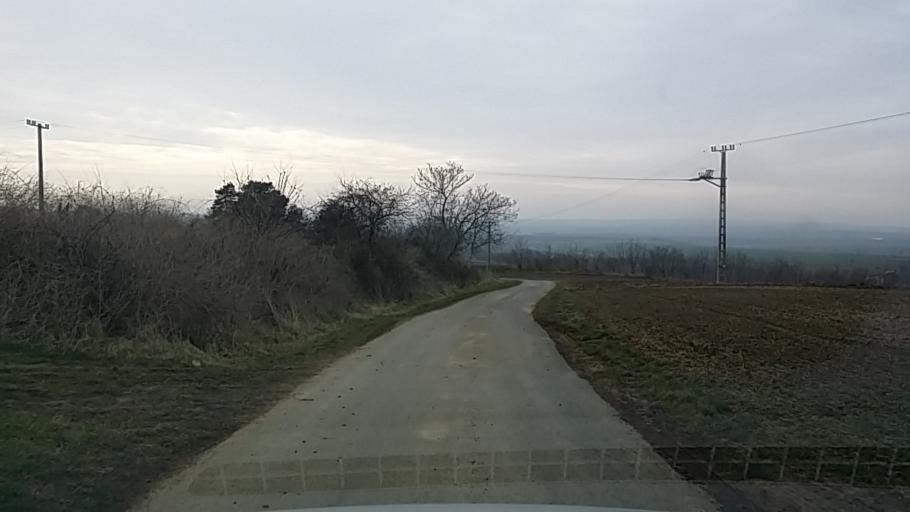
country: HU
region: Baranya
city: Pecsvarad
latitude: 46.1123
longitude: 18.5284
